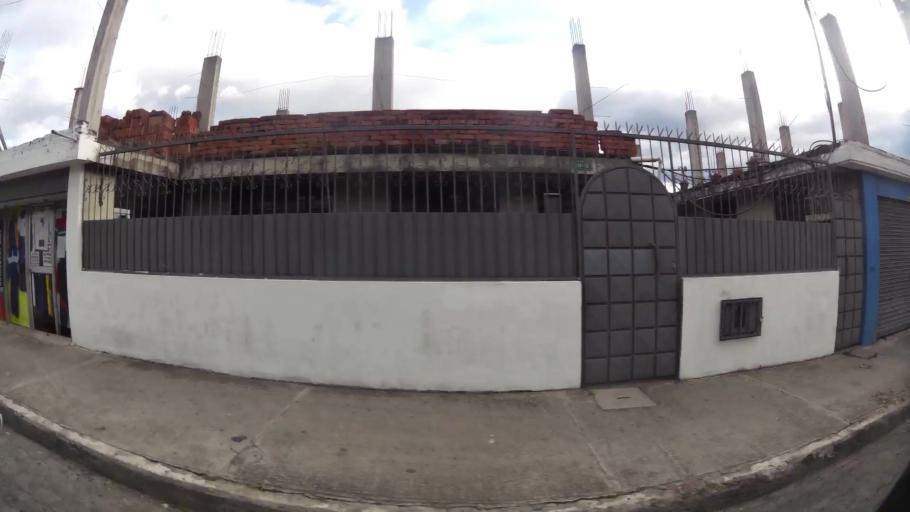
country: EC
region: Pichincha
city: Quito
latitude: -0.1495
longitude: -78.4655
